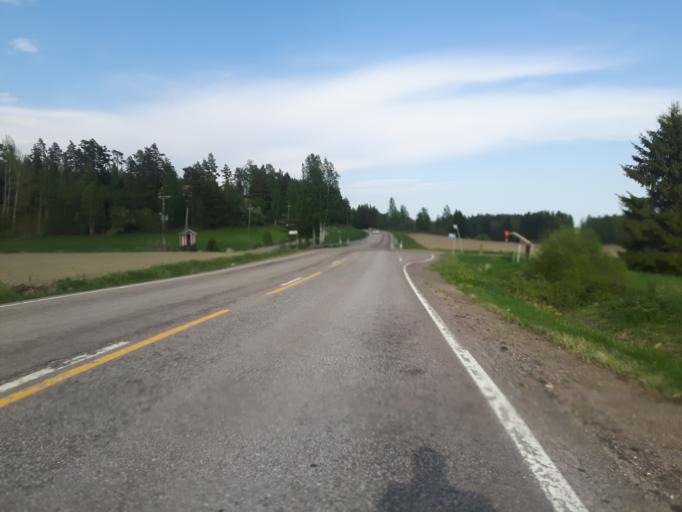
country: FI
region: Uusimaa
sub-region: Porvoo
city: Myrskylae
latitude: 60.4835
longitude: 25.8475
